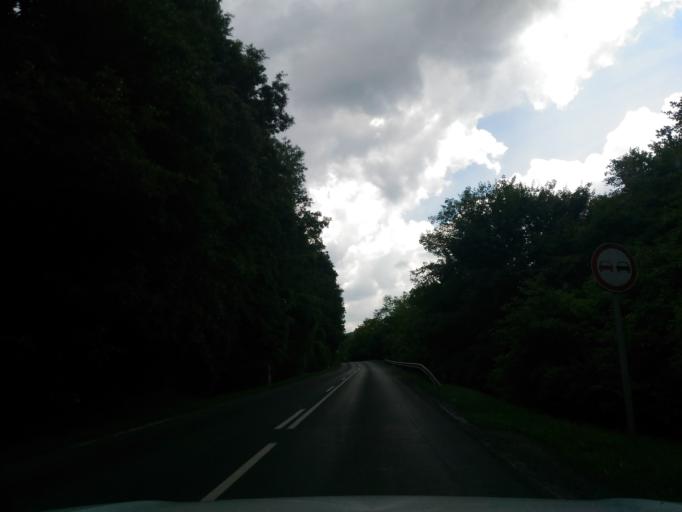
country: HU
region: Baranya
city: Komlo
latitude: 46.1785
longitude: 18.2098
